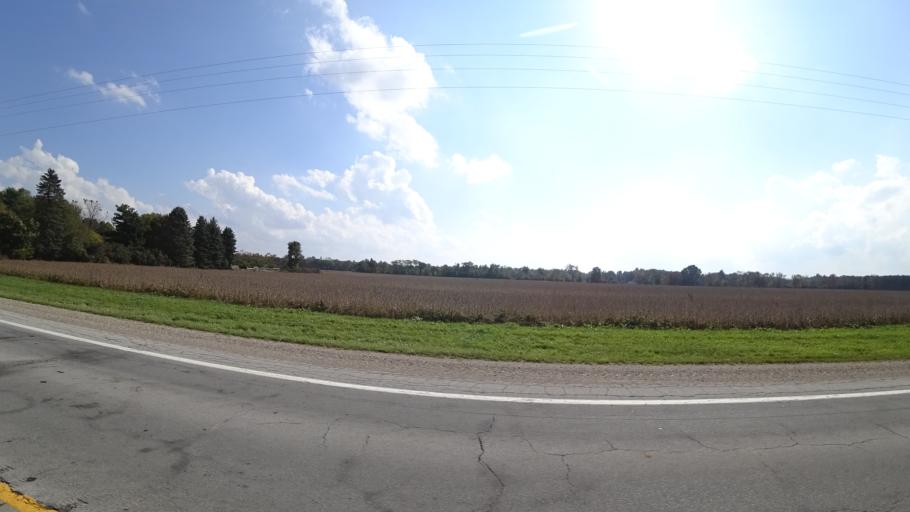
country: US
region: Michigan
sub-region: Saint Joseph County
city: Colon
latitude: 42.0102
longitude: -85.3779
